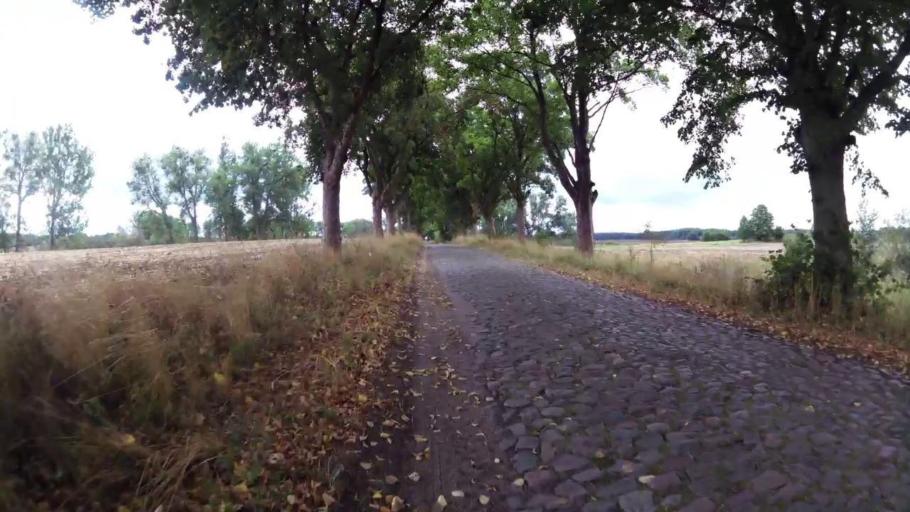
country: PL
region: West Pomeranian Voivodeship
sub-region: Powiat mysliborski
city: Debno
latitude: 52.8442
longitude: 14.7122
